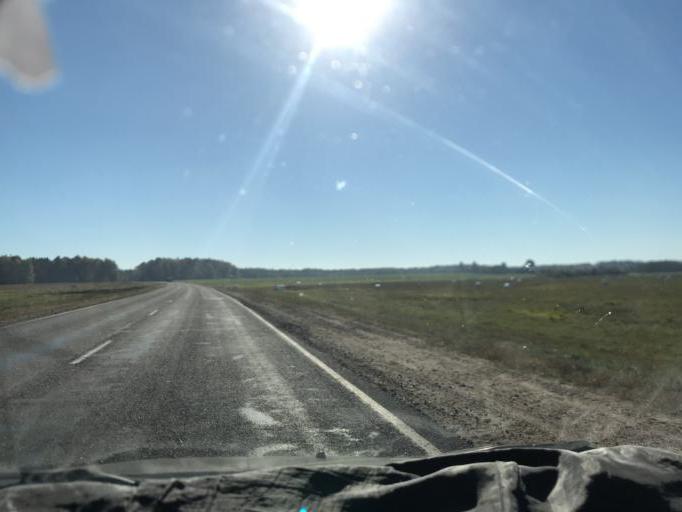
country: BY
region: Mogilev
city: Babruysk
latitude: 53.0624
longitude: 29.0827
